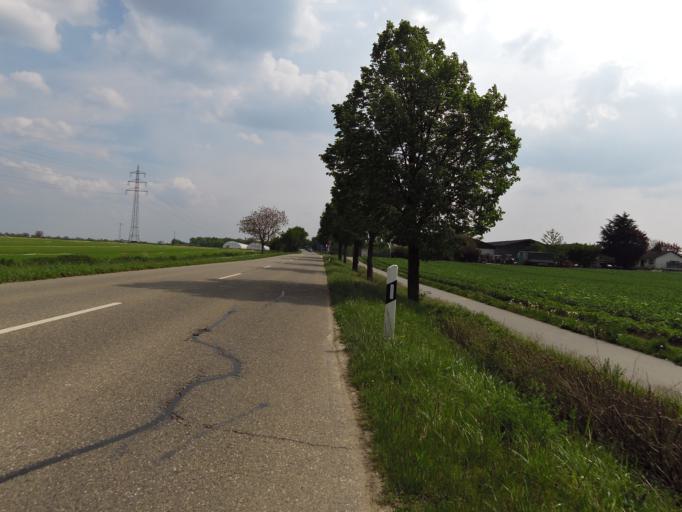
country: DE
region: Rheinland-Pfalz
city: Meckenheim
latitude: 49.3875
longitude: 8.2471
